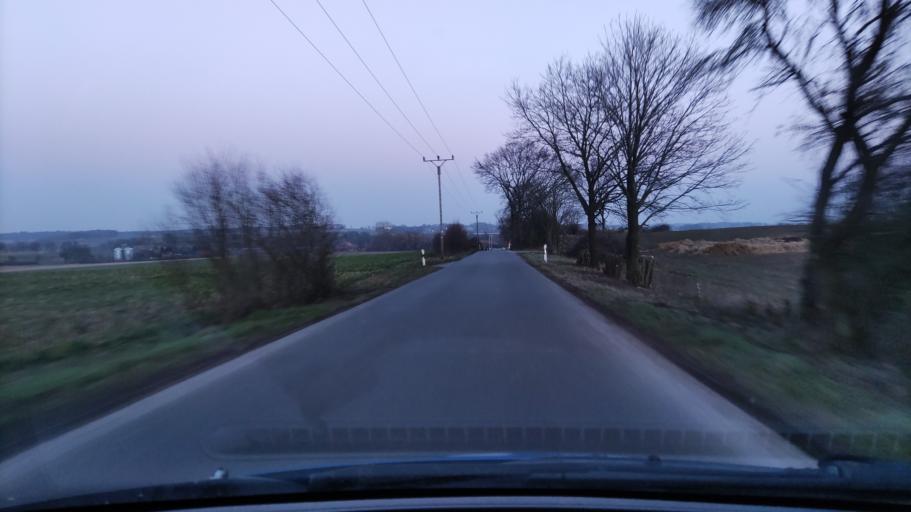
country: DE
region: Lower Saxony
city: Barum
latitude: 53.0537
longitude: 10.5004
